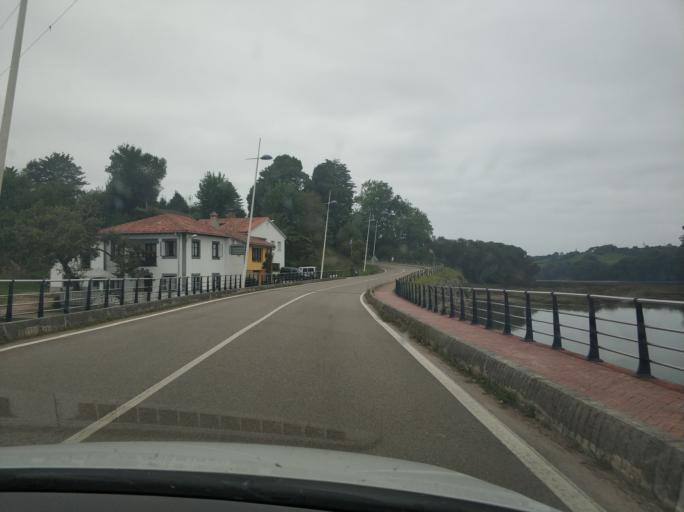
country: ES
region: Cantabria
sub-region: Provincia de Cantabria
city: Comillas
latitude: 43.3805
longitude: -4.3178
